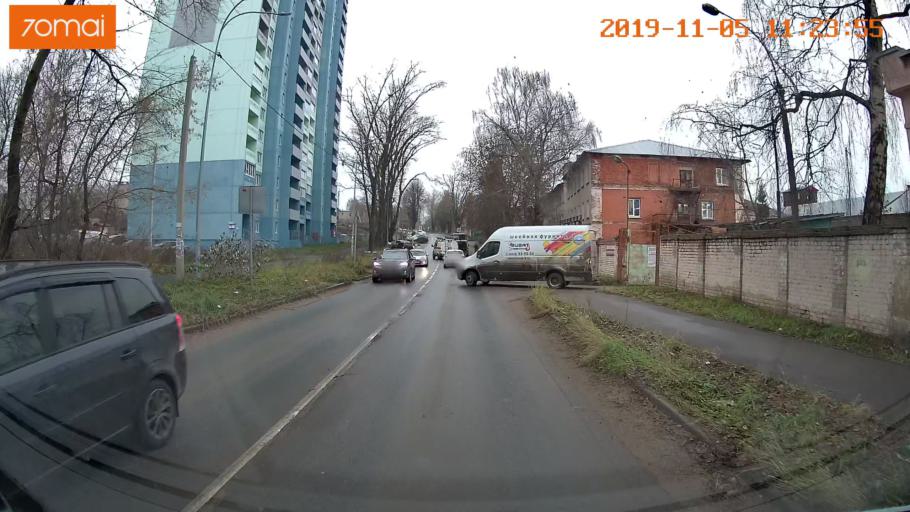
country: RU
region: Ivanovo
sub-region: Gorod Ivanovo
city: Ivanovo
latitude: 57.0042
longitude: 40.9637
